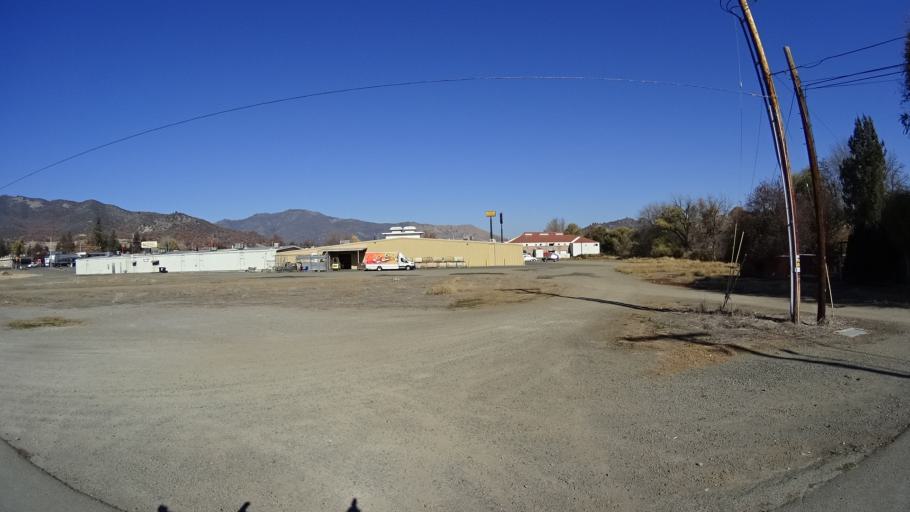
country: US
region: California
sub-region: Siskiyou County
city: Yreka
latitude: 41.7384
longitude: -122.6322
